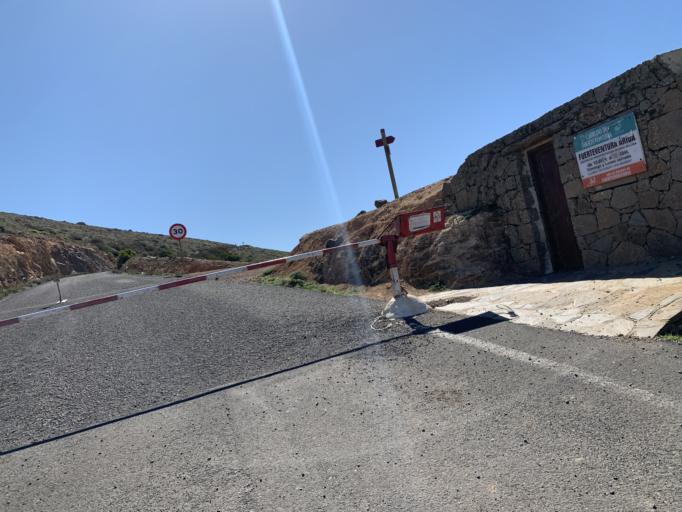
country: ES
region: Canary Islands
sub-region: Provincia de Las Palmas
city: Antigua
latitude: 28.4400
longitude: -14.0541
